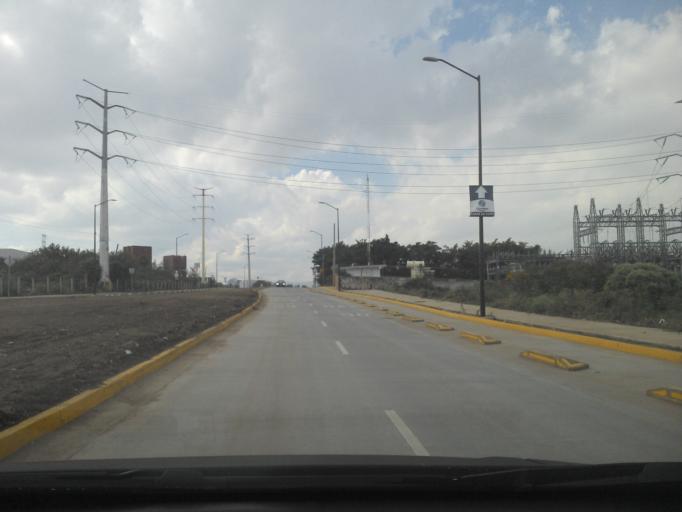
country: MX
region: Jalisco
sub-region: Tlajomulco de Zuniga
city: Altus Bosques
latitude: 20.6147
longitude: -103.3607
